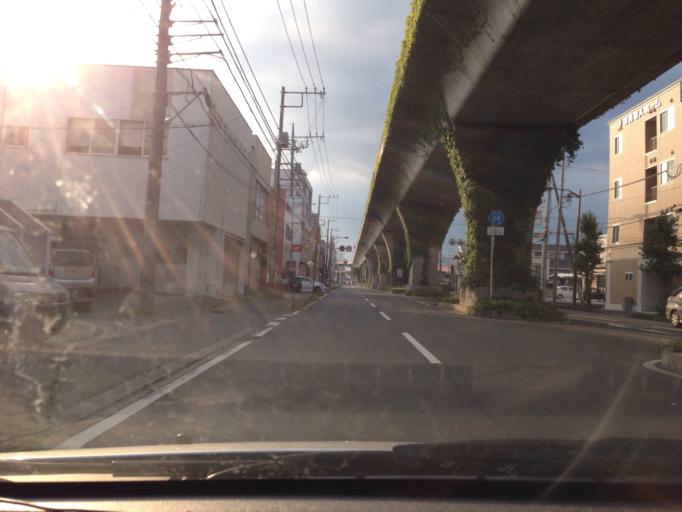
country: JP
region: Ibaraki
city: Naka
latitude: 36.0830
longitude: 140.1919
